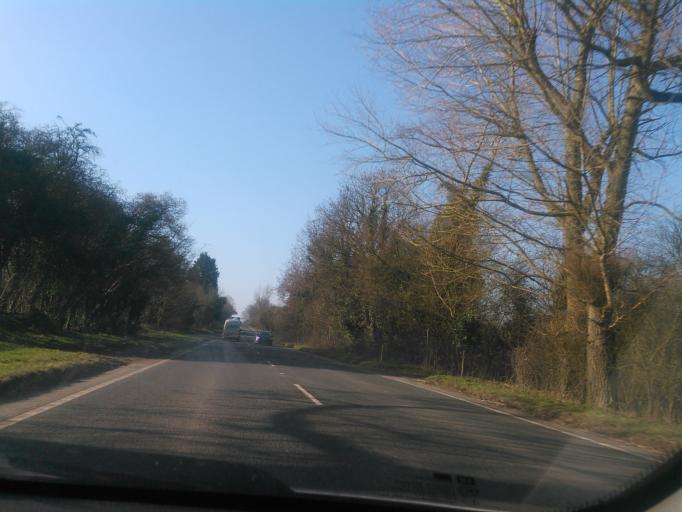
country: GB
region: England
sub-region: Shropshire
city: Church Stretton
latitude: 52.5539
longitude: -2.7879
